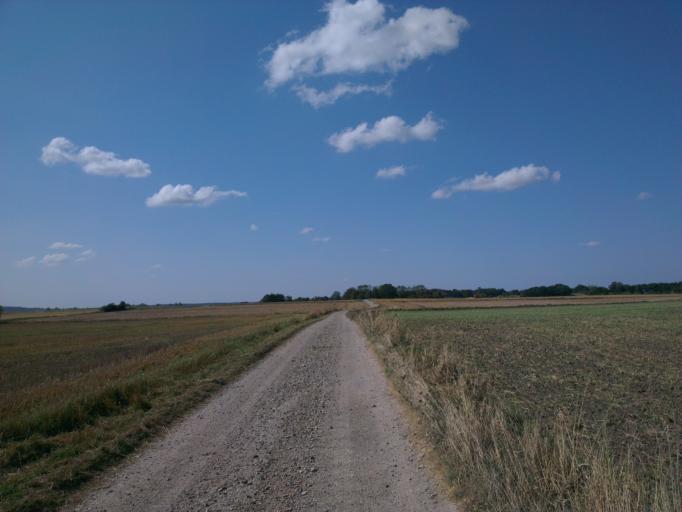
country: DK
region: Capital Region
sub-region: Frederikssund Kommune
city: Frederikssund
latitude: 55.8781
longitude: 12.0897
